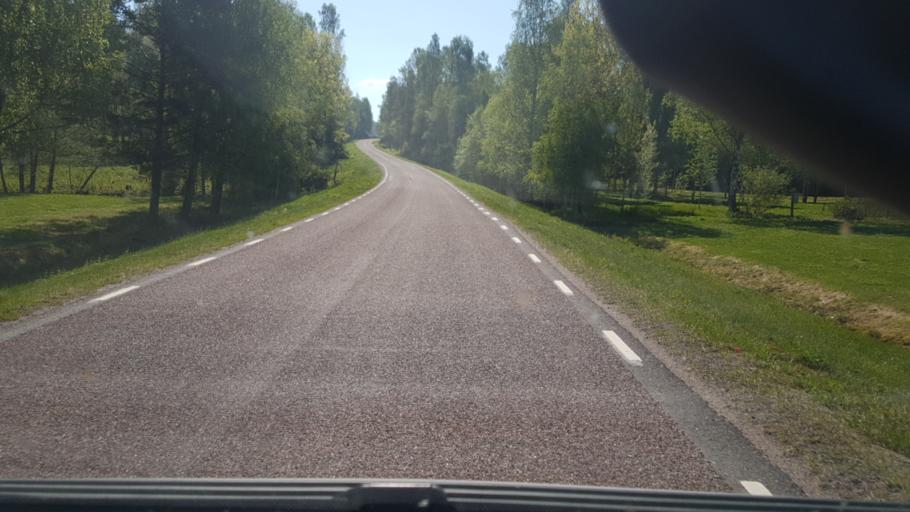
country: NO
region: Hedmark
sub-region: Eidskog
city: Skotterud
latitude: 59.7906
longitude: 12.0291
